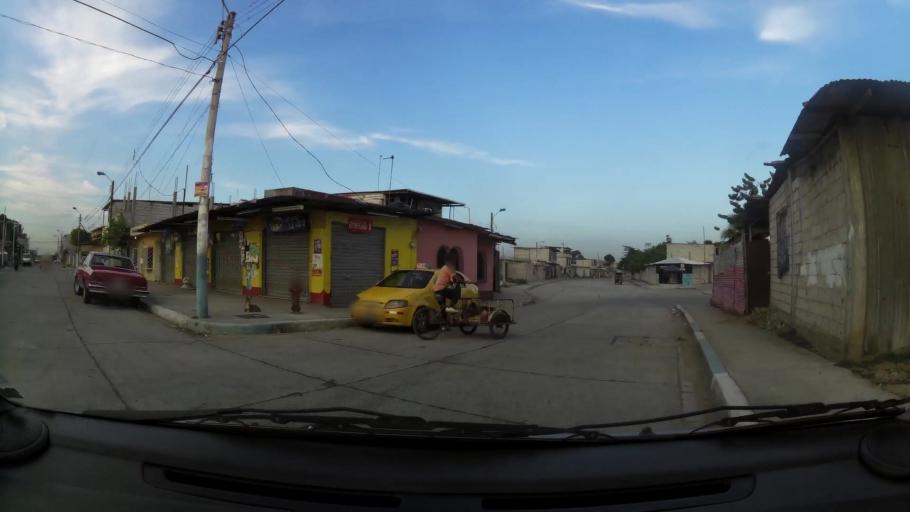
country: EC
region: Guayas
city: Eloy Alfaro
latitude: -2.0892
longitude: -79.8978
